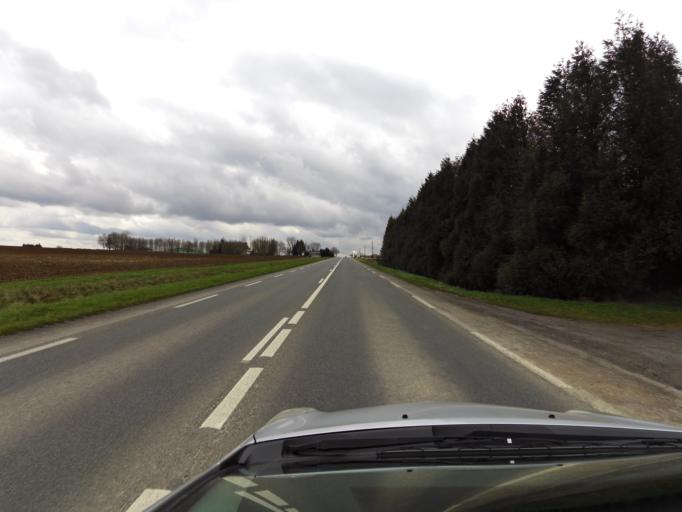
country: FR
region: Nord-Pas-de-Calais
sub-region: Departement du Pas-de-Calais
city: Beaurains
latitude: 50.2407
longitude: 2.7981
